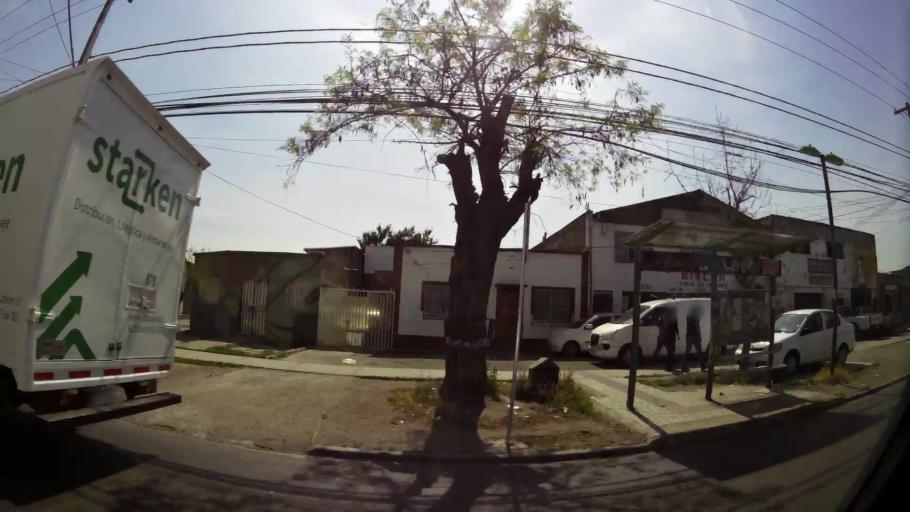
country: CL
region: Santiago Metropolitan
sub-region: Provincia de Santiago
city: Lo Prado
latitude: -33.4277
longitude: -70.7084
